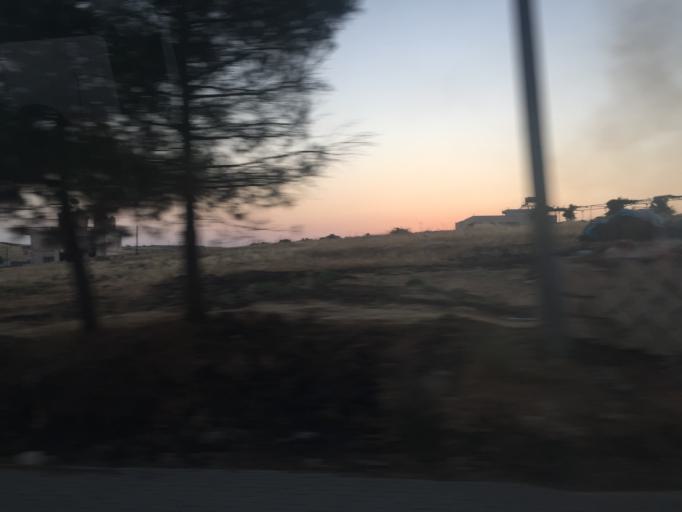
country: TR
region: Mardin
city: Kindirip
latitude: 37.4602
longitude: 41.2250
